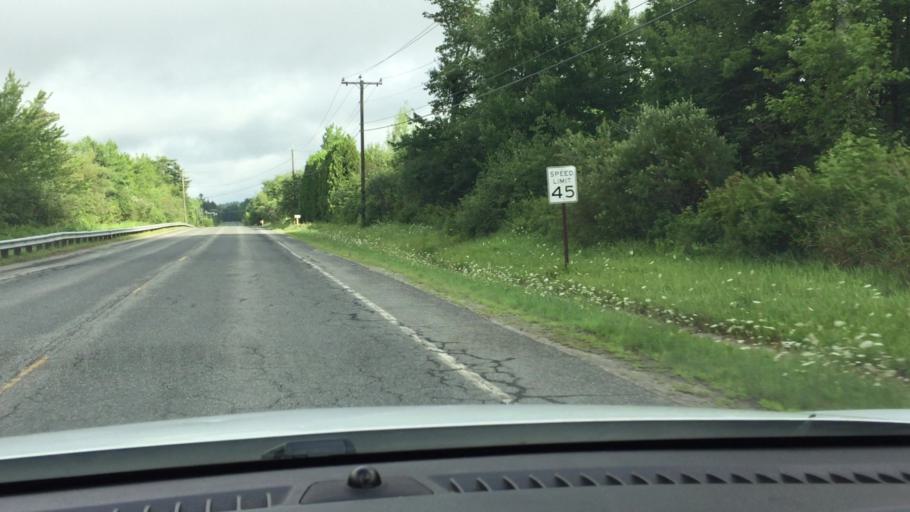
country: US
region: Massachusetts
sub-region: Berkshire County
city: Hinsdale
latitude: 42.4395
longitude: -73.0484
